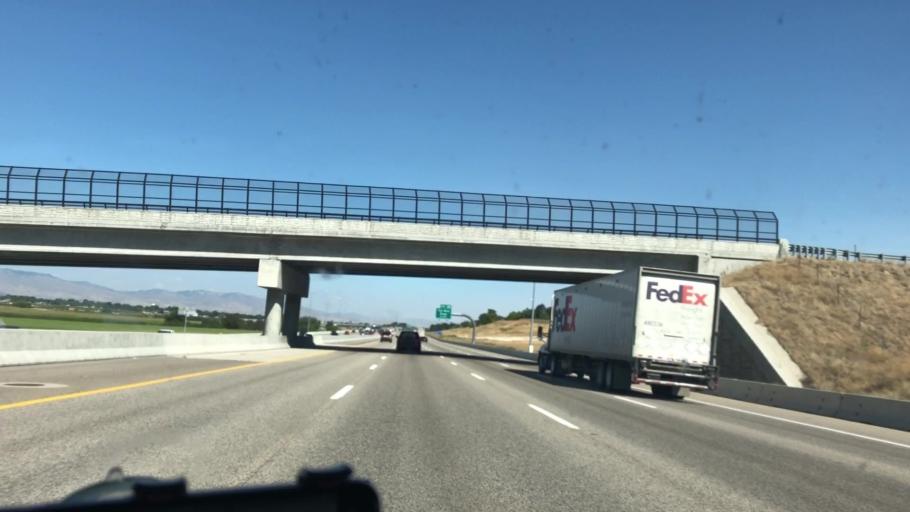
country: US
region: Idaho
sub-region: Ada County
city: Meridian
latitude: 43.5948
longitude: -116.4545
